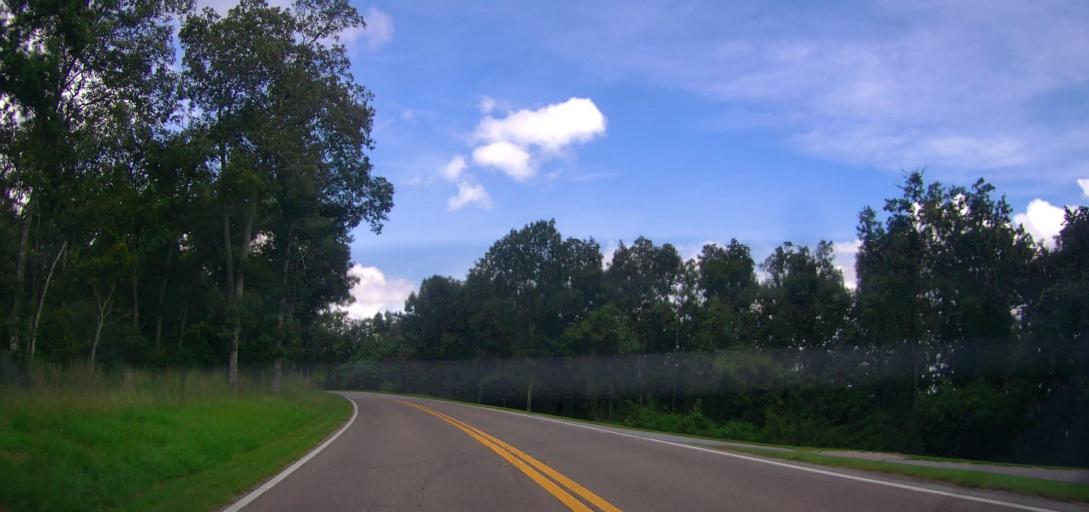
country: US
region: Georgia
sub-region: Harris County
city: Pine Mountain
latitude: 32.8460
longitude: -84.7798
